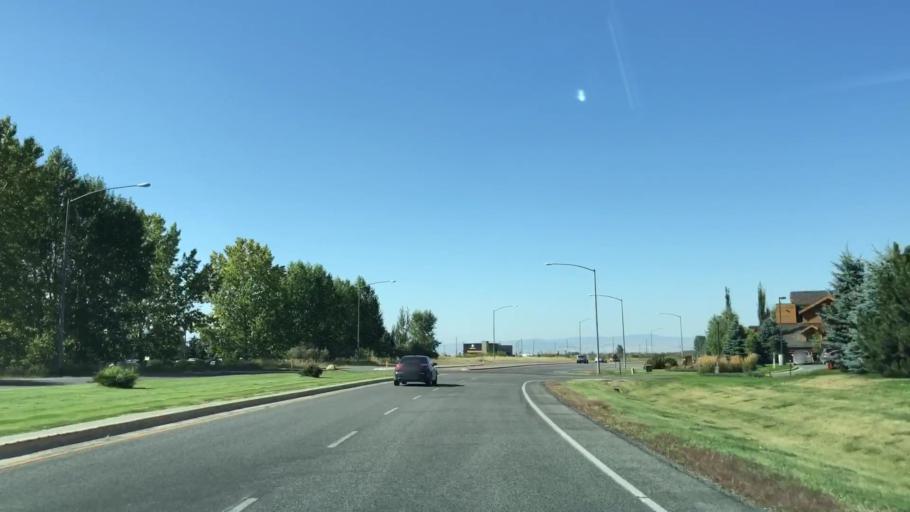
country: US
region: Montana
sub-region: Gallatin County
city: Bozeman
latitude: 45.7128
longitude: -111.0673
